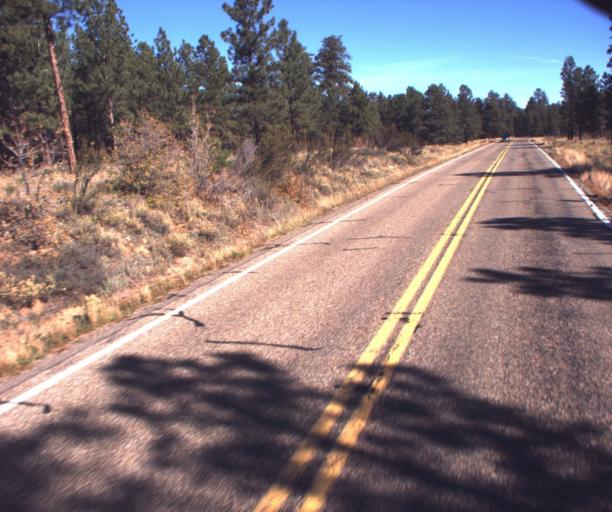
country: US
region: Arizona
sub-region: Coconino County
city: Fredonia
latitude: 36.7596
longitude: -112.2656
